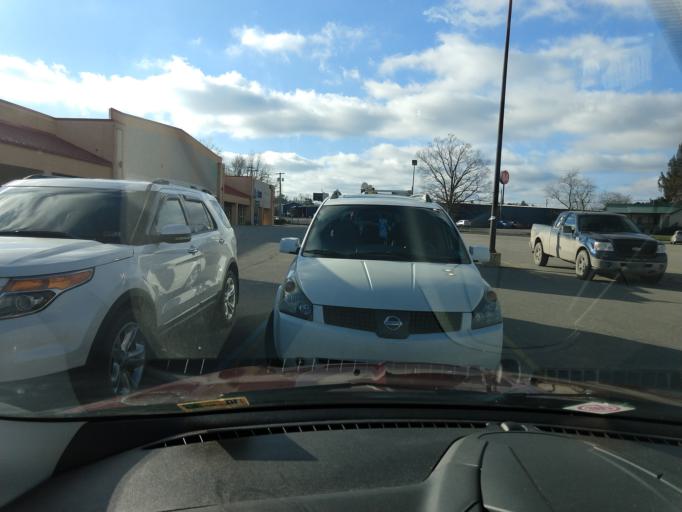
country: US
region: West Virginia
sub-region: Randolph County
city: Elkins
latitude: 38.8900
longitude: -79.8446
